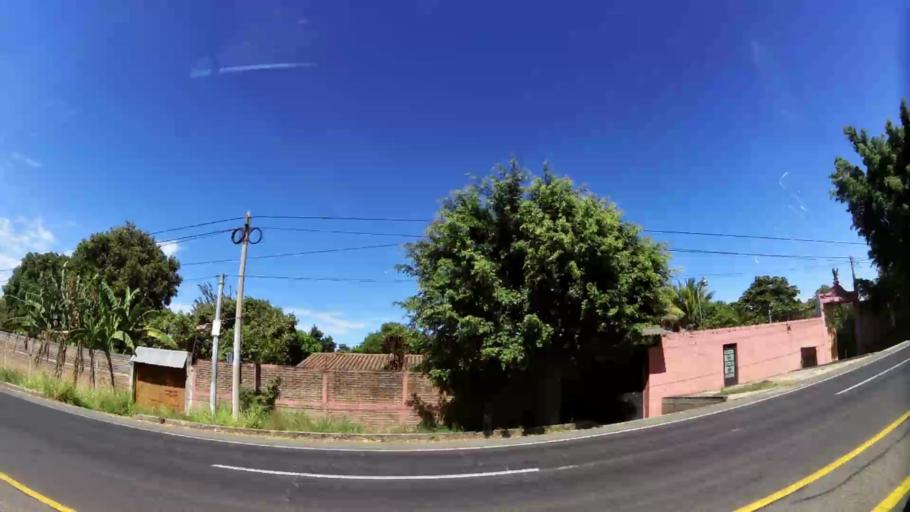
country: SV
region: Santa Ana
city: Chalchuapa
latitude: 13.9729
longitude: -89.7084
